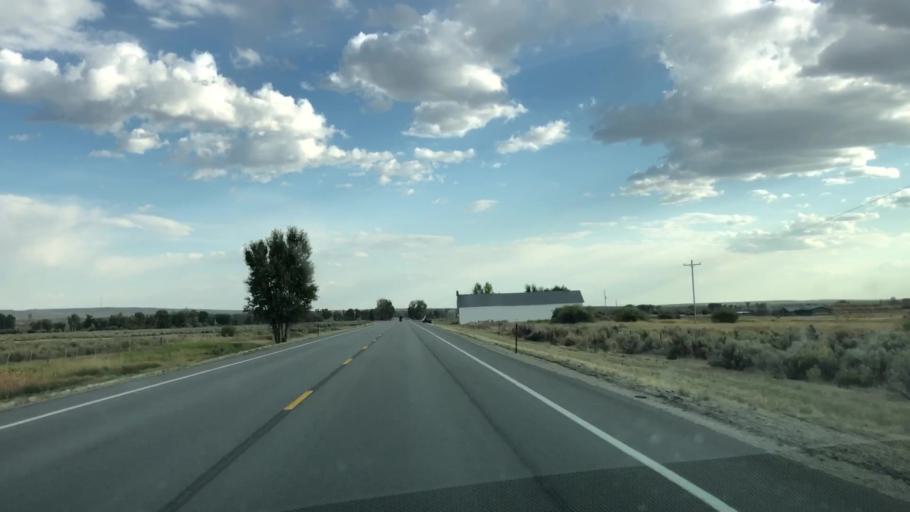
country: US
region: Wyoming
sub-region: Sublette County
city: Pinedale
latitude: 42.7051
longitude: -109.7134
